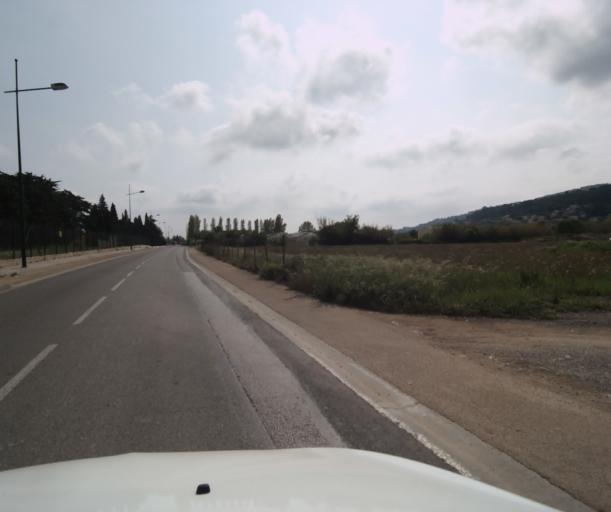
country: FR
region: Provence-Alpes-Cote d'Azur
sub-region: Departement du Var
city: Hyeres
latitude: 43.1001
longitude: 6.1387
